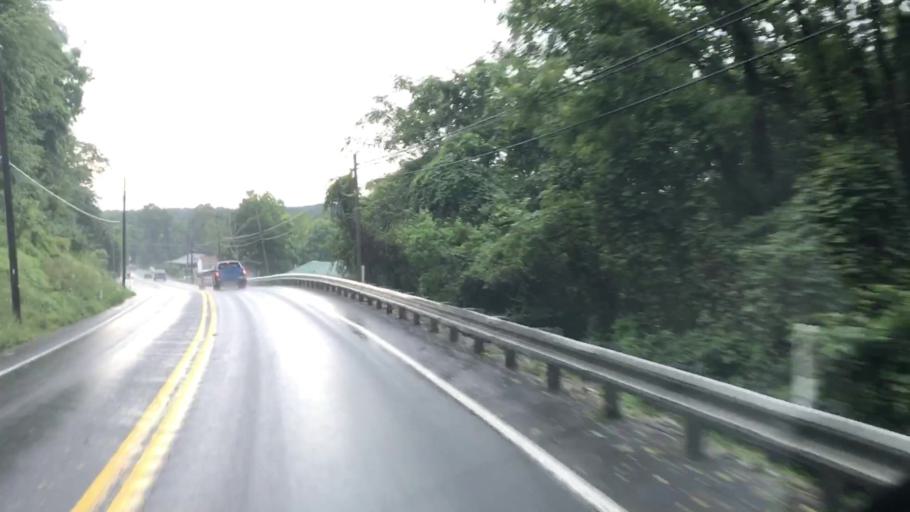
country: US
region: Pennsylvania
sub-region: Cumberland County
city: Schlusser
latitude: 40.2967
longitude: -77.1343
